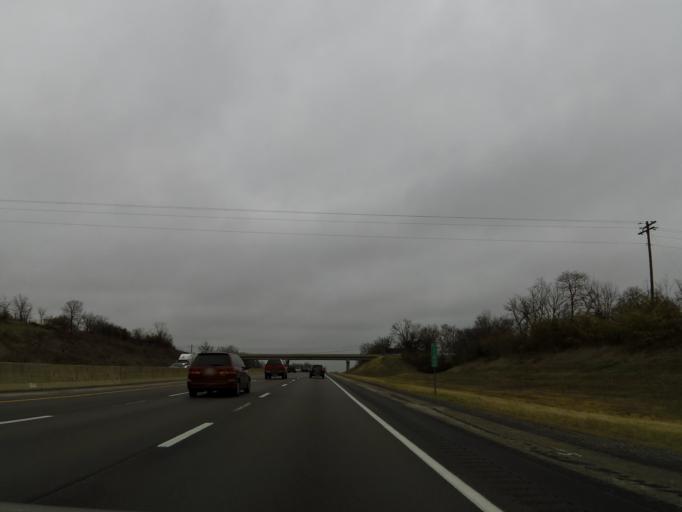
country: US
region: Kentucky
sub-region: Grant County
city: Crittenden
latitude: 38.7343
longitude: -84.6048
